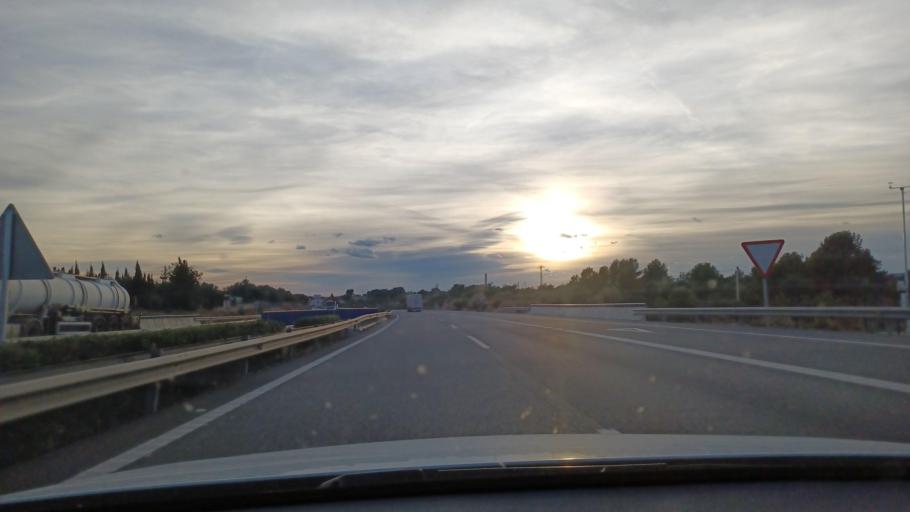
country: ES
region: Catalonia
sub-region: Provincia de Tarragona
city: L'Ampolla
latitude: 40.8126
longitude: 0.7012
